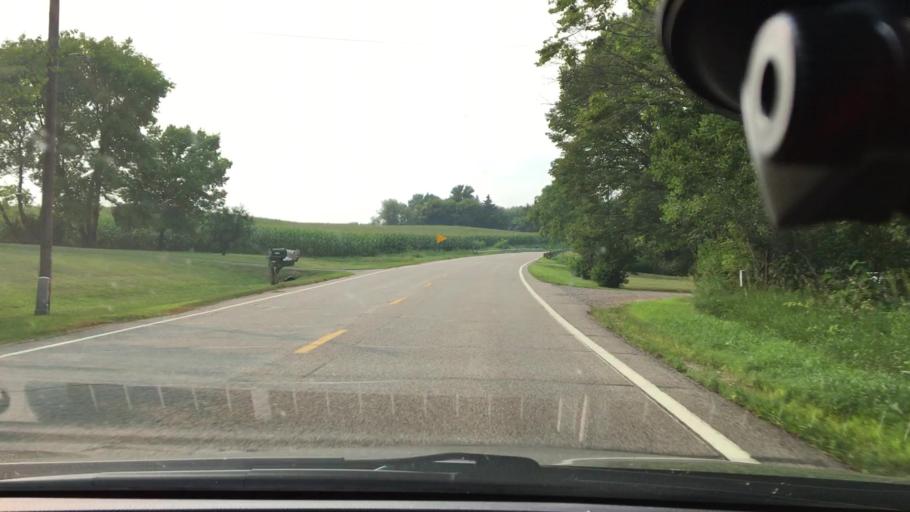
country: US
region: Minnesota
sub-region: Hennepin County
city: Dayton
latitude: 45.2249
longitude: -93.4879
